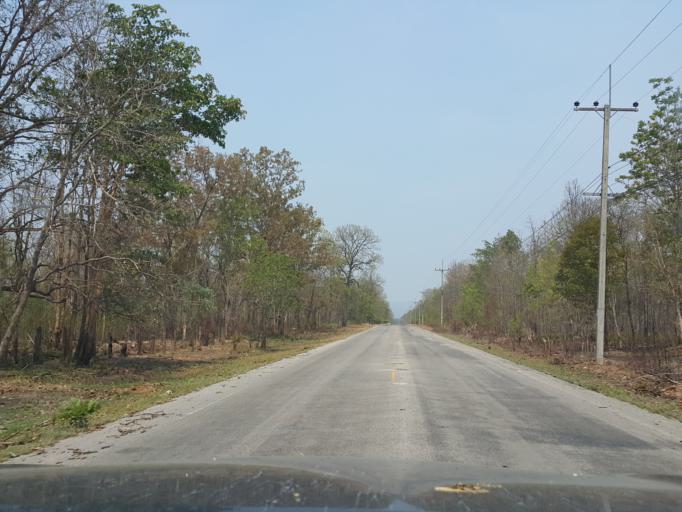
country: TH
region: Lampang
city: Mae Phrik
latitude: 17.5541
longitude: 99.1112
